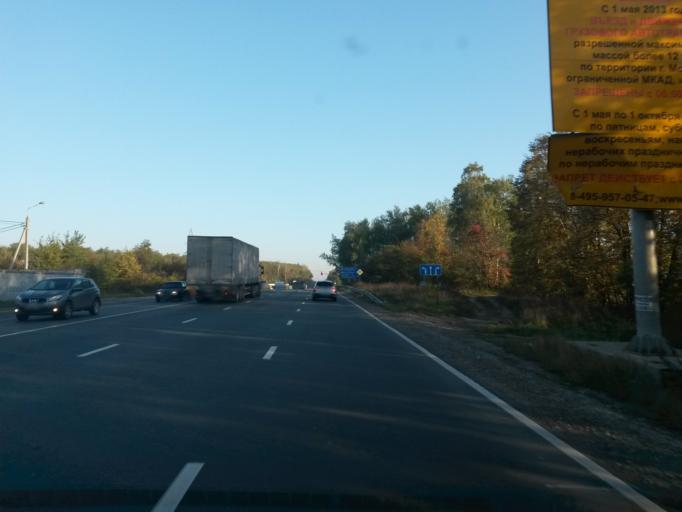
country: RU
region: Moskovskaya
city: Belyye Stolby
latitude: 55.3366
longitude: 37.8023
